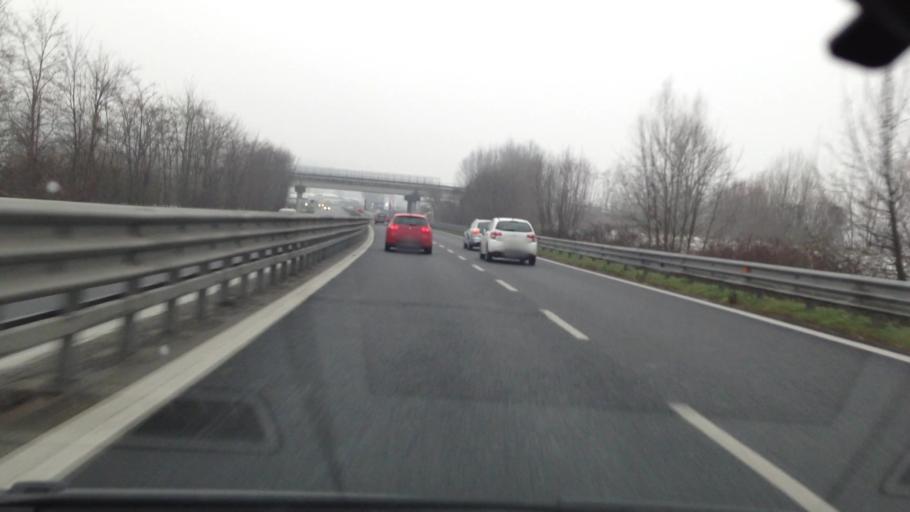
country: IT
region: Piedmont
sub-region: Provincia di Asti
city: Mongardino
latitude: 44.8685
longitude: 8.2063
